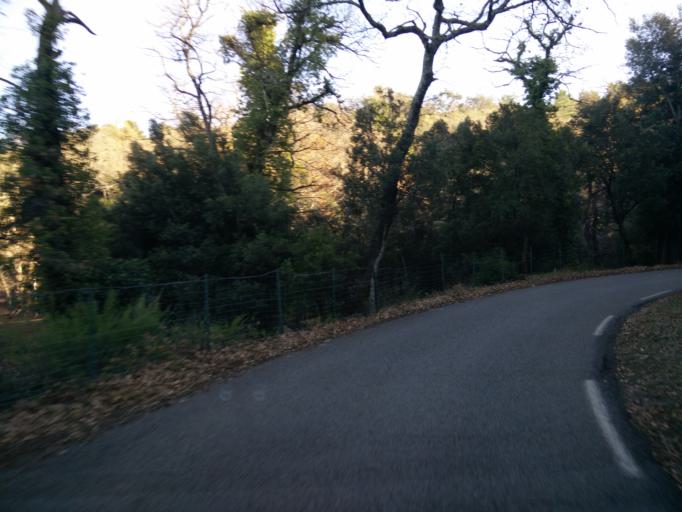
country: FR
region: Provence-Alpes-Cote d'Azur
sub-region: Departement du Var
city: Collobrieres
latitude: 43.2179
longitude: 6.2955
